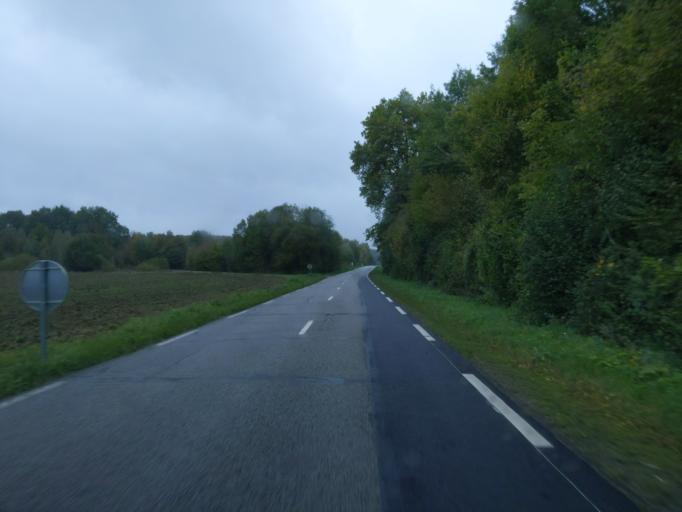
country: FR
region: Ile-de-France
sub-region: Departement des Yvelines
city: Dampierre-en-Yvelines
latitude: 48.6933
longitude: 1.9759
